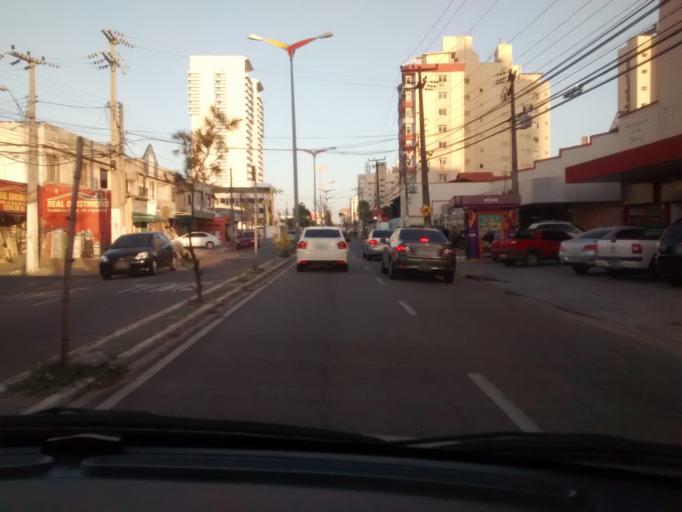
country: BR
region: Ceara
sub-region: Fortaleza
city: Fortaleza
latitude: -3.7412
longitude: -38.4829
